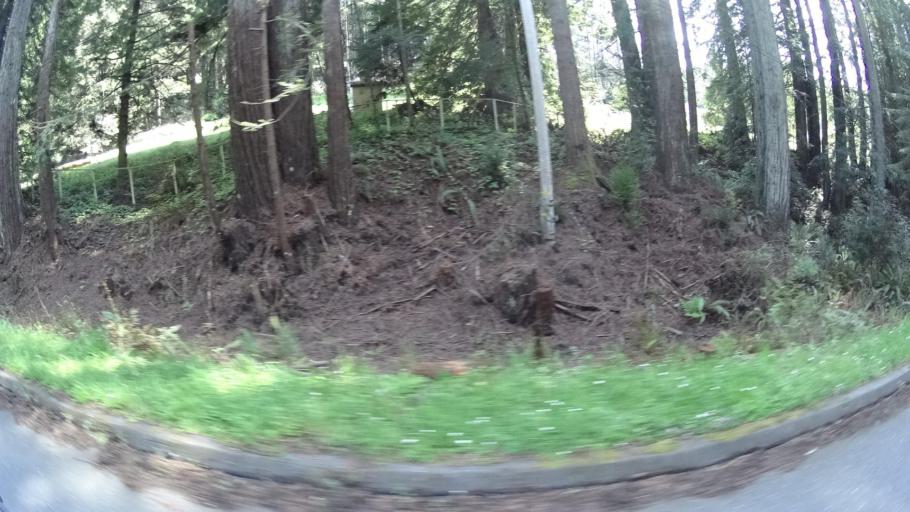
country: US
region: California
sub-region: Humboldt County
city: Hydesville
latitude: 40.5693
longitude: -124.1129
